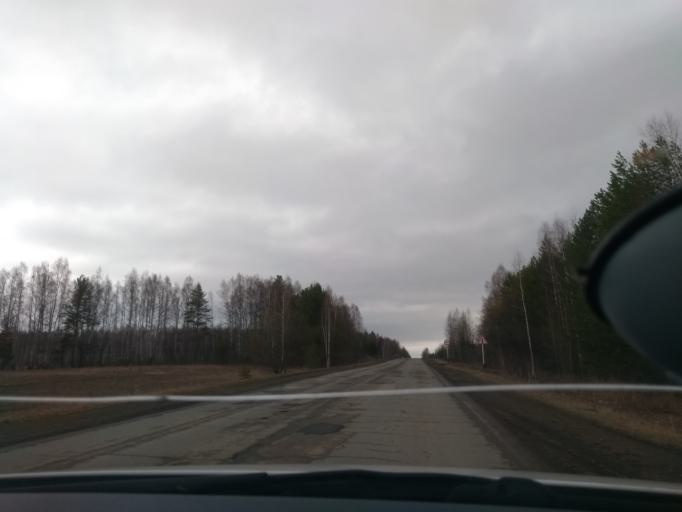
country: RU
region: Perm
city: Kungur
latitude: 57.3627
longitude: 56.8199
